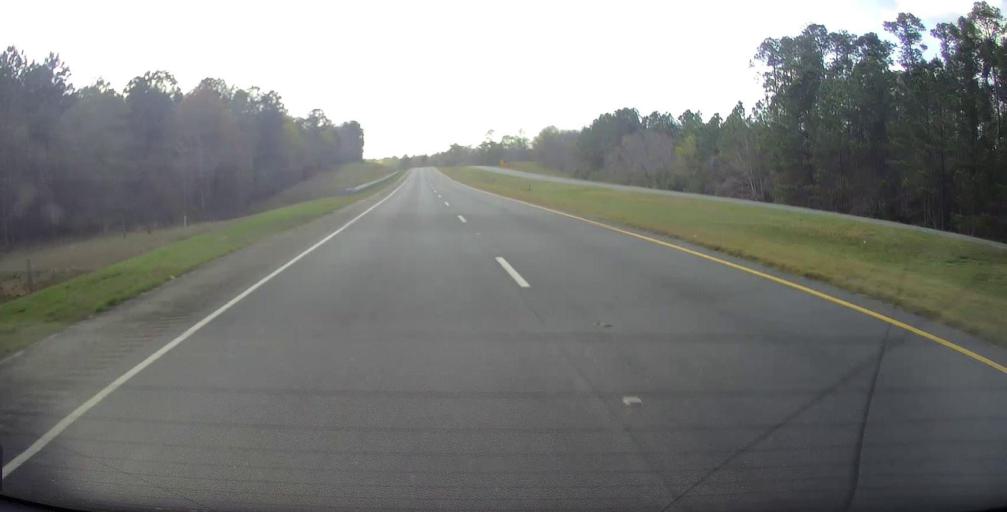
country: US
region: Georgia
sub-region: Telfair County
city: Helena
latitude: 32.1048
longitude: -82.9715
